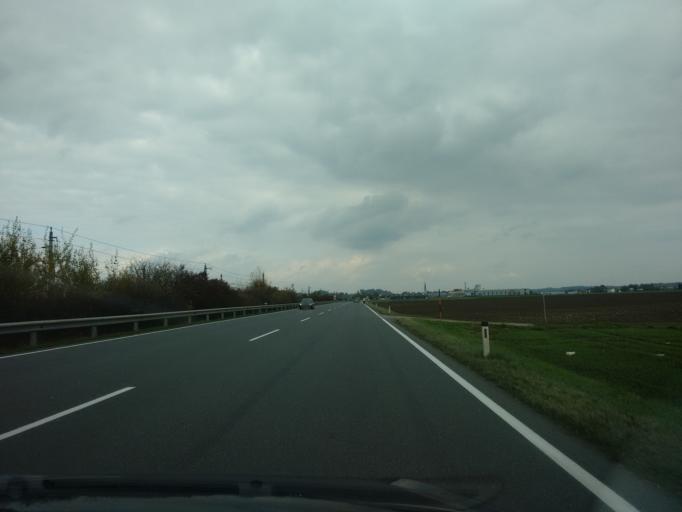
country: AT
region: Upper Austria
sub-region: Politischer Bezirk Vocklabruck
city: Oberndorf bei Schwanenstadt
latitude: 48.0410
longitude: 13.7491
